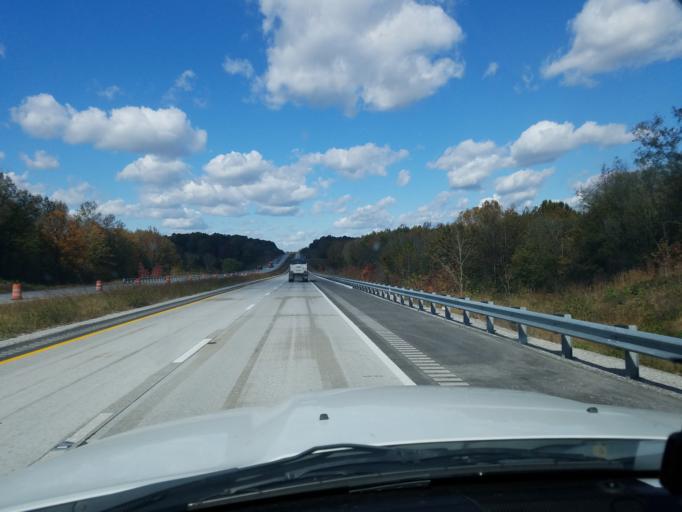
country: US
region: Kentucky
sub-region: Ohio County
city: Oak Grove
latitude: 37.3164
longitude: -86.7414
